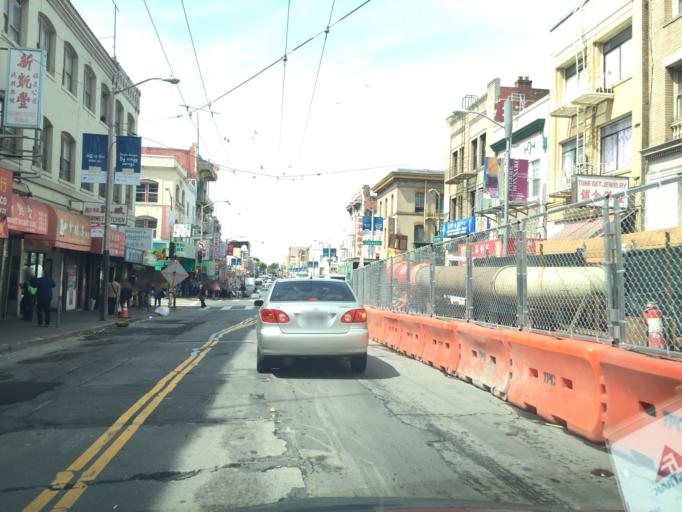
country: US
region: California
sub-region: San Francisco County
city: San Francisco
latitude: 37.7953
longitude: -122.4082
